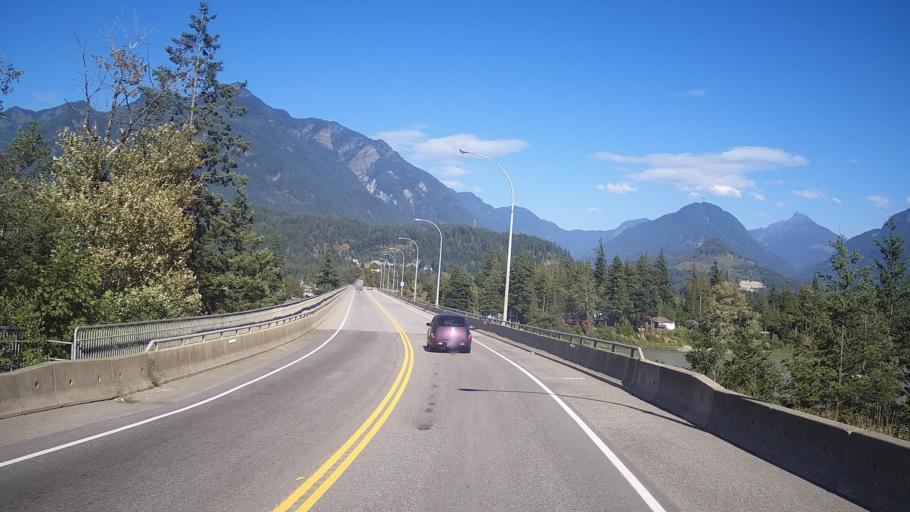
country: CA
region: British Columbia
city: Hope
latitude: 49.3860
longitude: -121.4549
